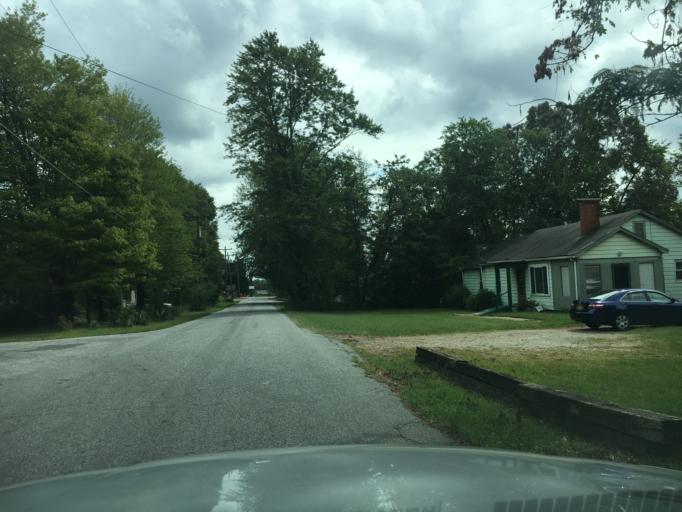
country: US
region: North Carolina
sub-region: Catawba County
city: Hickory
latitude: 35.7179
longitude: -81.3353
